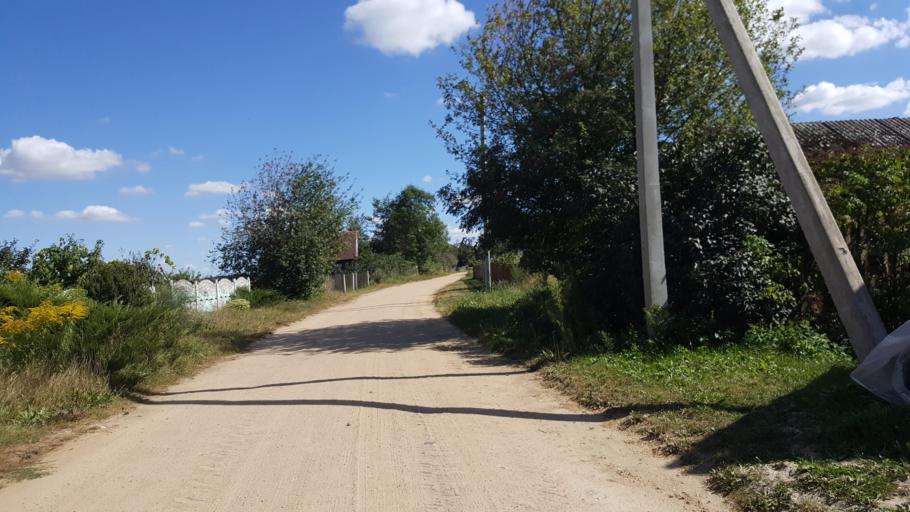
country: BY
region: Brest
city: Vysokaye
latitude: 52.2581
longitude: 23.4241
